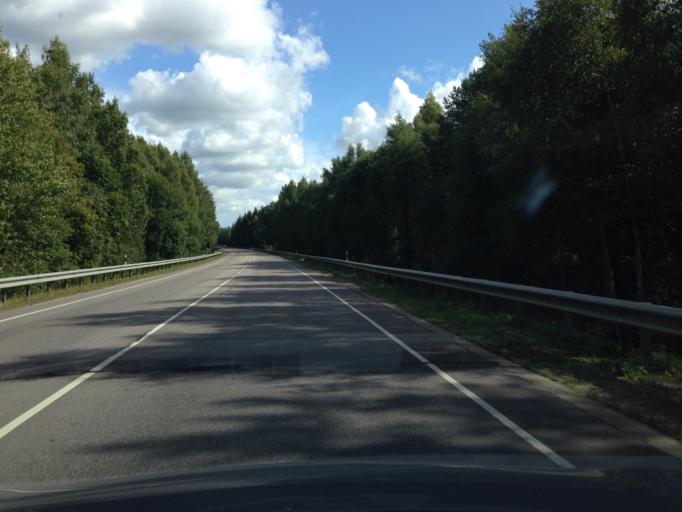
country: EE
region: Harju
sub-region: Saku vald
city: Saku
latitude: 59.3125
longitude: 24.6933
